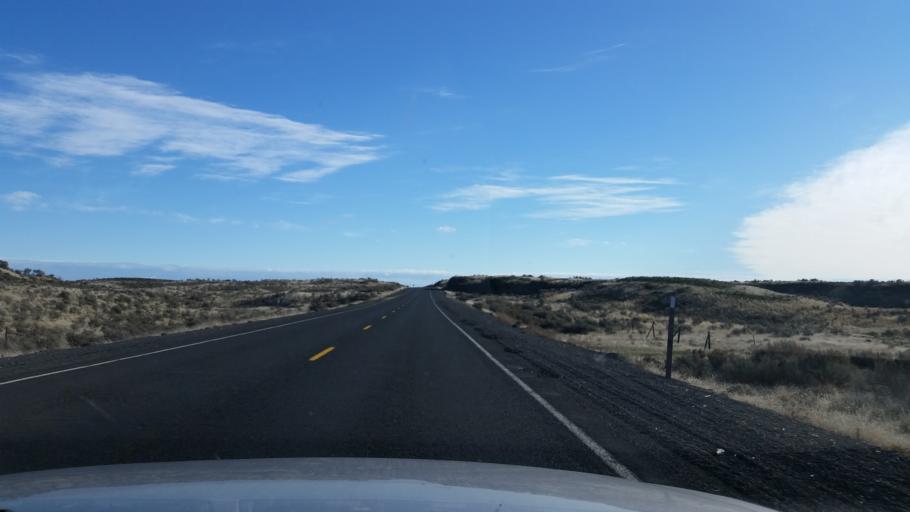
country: US
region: Washington
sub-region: Grant County
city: Warden
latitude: 47.3244
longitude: -118.8672
